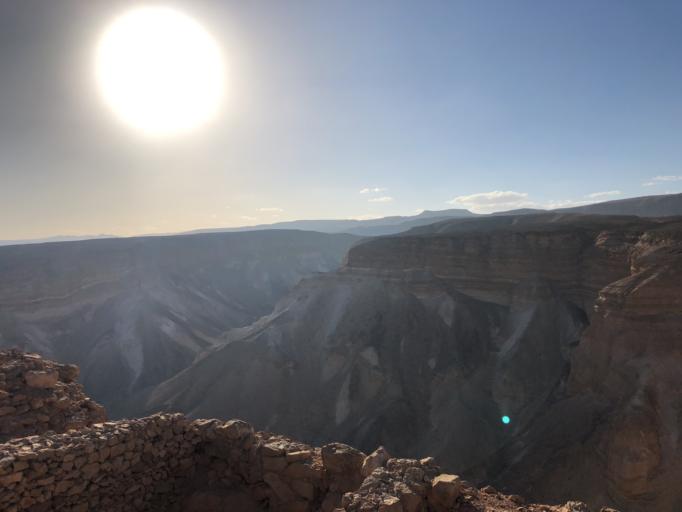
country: IL
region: Southern District
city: `En Boqeq
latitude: 31.3132
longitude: 35.3526
